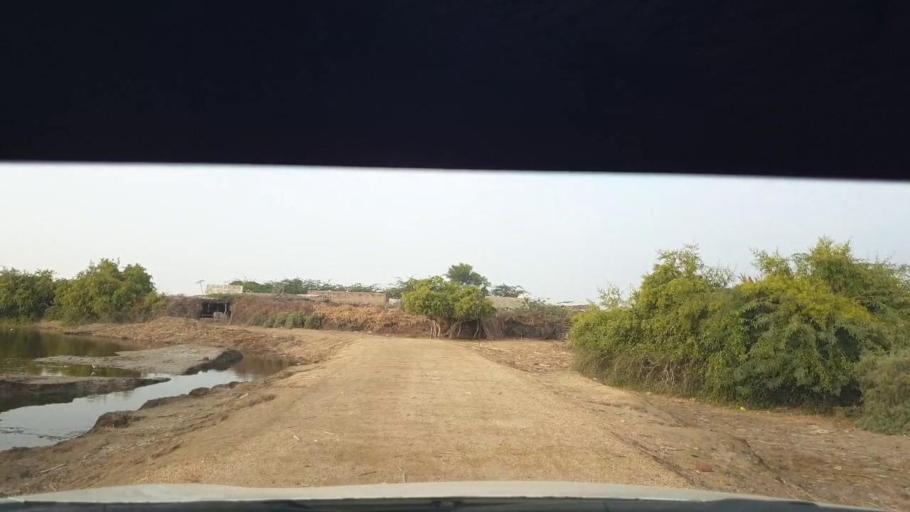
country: PK
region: Sindh
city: Berani
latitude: 25.7500
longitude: 68.9497
